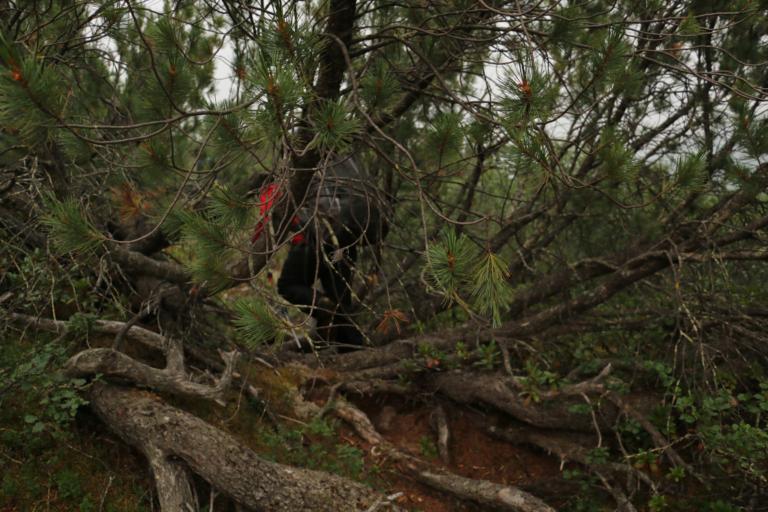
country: RU
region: Respublika Buryatiya
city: Kichera
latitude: 56.2367
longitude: 110.5847
